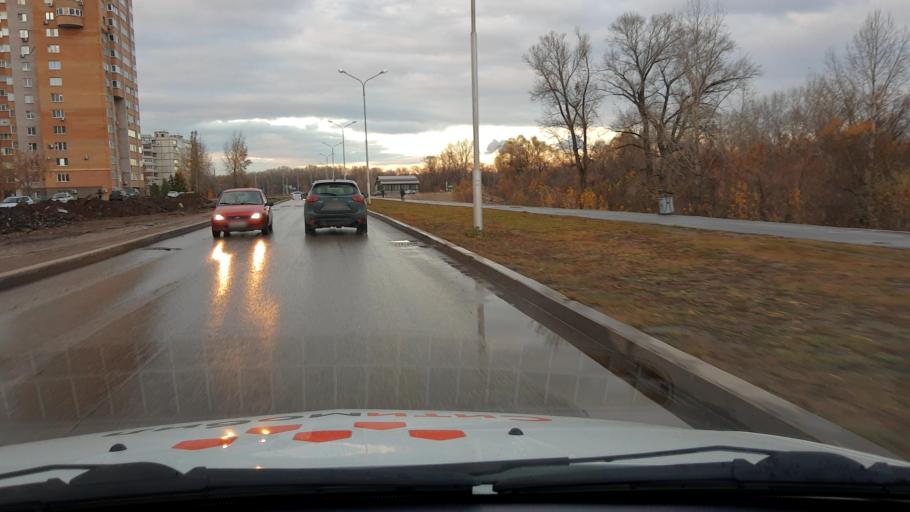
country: RU
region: Bashkortostan
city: Ufa
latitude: 54.7711
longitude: 56.0850
